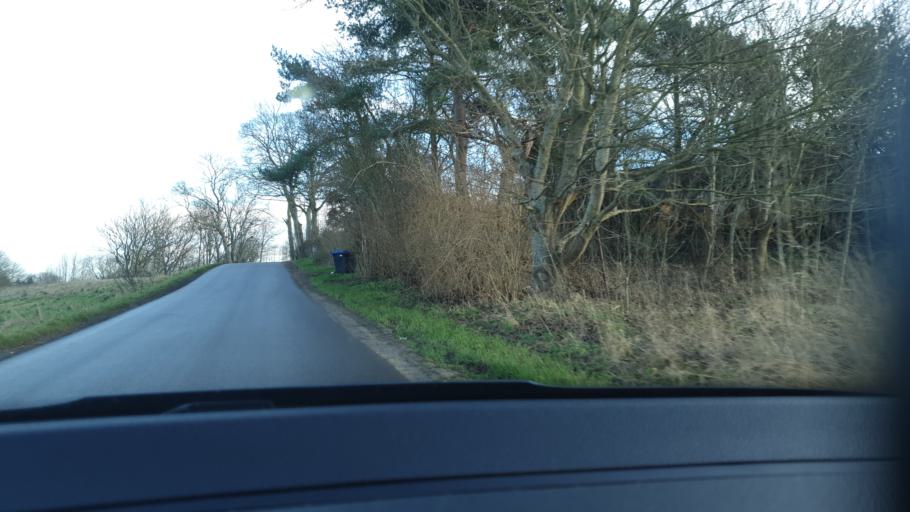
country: DK
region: Zealand
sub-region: Odsherred Kommune
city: Hojby
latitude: 55.9191
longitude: 11.6287
